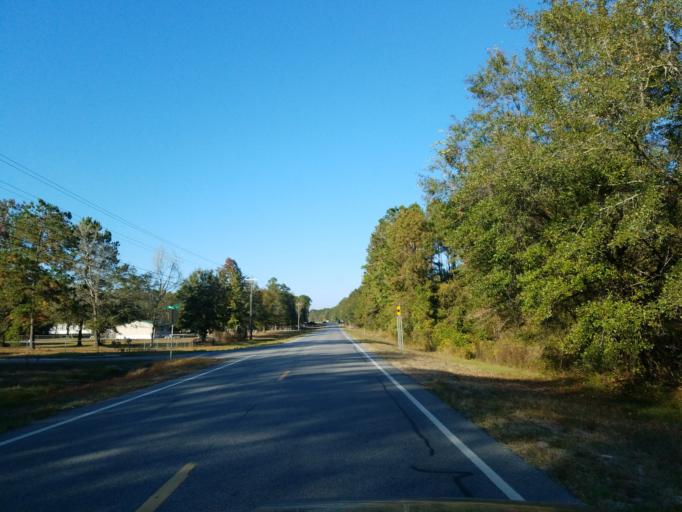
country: US
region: Georgia
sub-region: Echols County
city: Statenville
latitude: 30.7032
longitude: -83.0616
